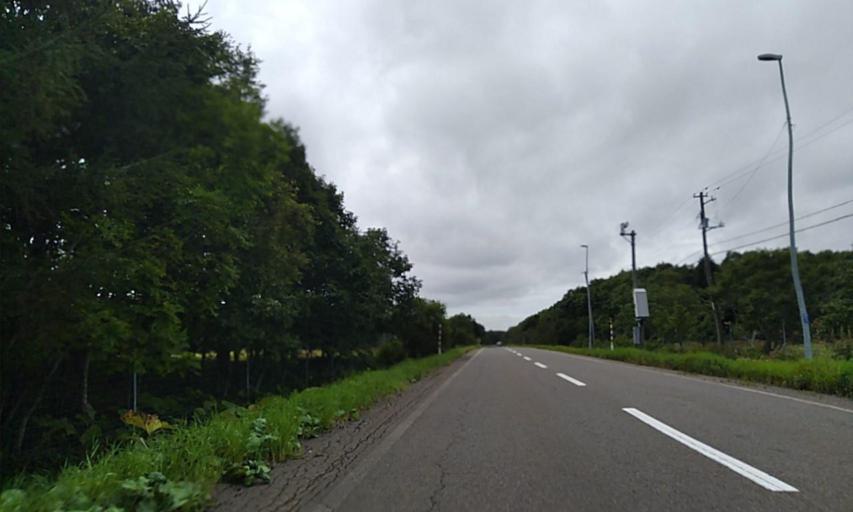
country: JP
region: Hokkaido
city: Nemuro
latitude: 43.3639
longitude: 145.2757
